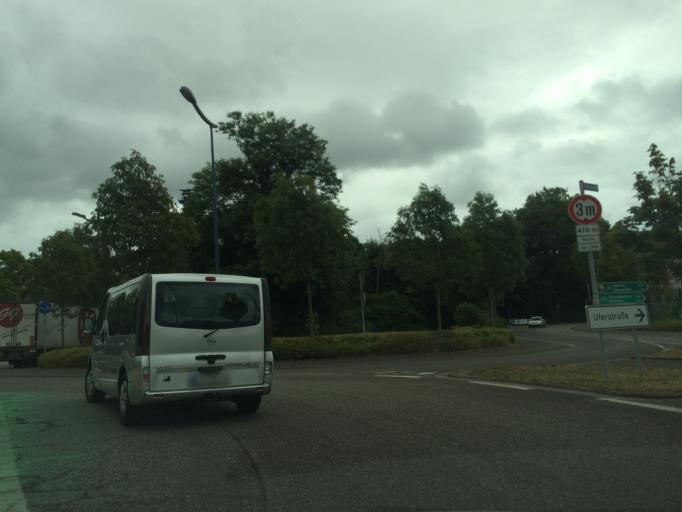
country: DE
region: Saarland
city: Dillingen
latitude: 49.3505
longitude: 6.7311
